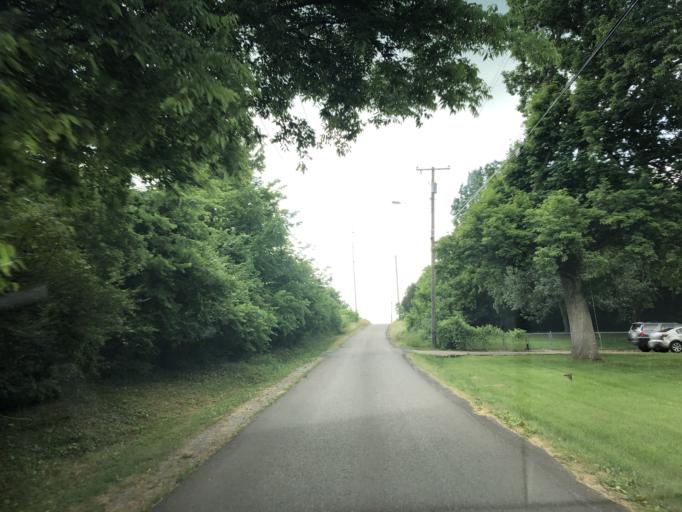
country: US
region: Tennessee
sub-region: Davidson County
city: Goodlettsville
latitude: 36.2763
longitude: -86.7026
